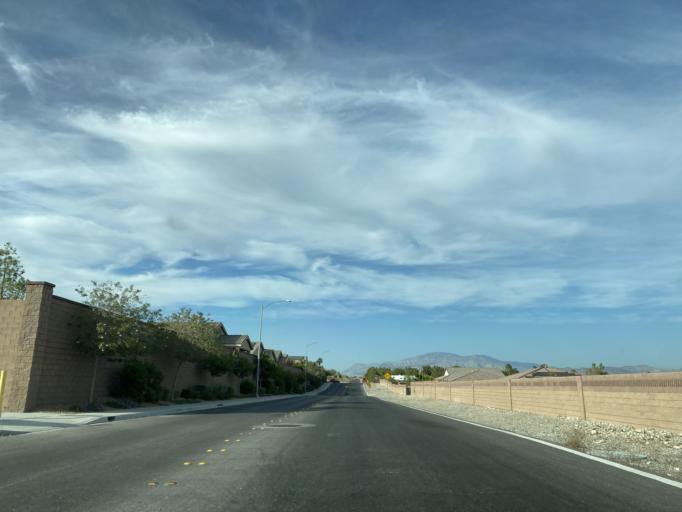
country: US
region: Nevada
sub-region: Clark County
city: Summerlin South
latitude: 36.2864
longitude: -115.3126
